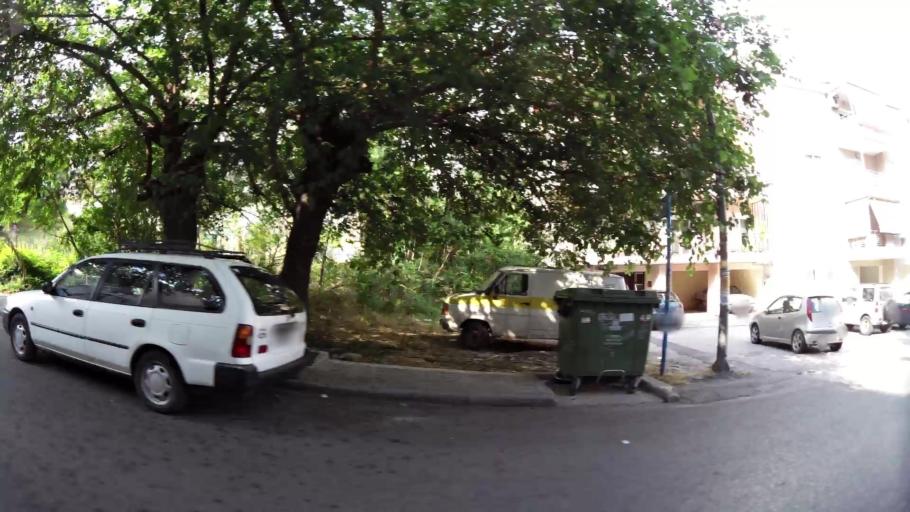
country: GR
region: Central Macedonia
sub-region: Nomos Thessalonikis
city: Sykies
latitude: 40.6457
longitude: 22.9526
